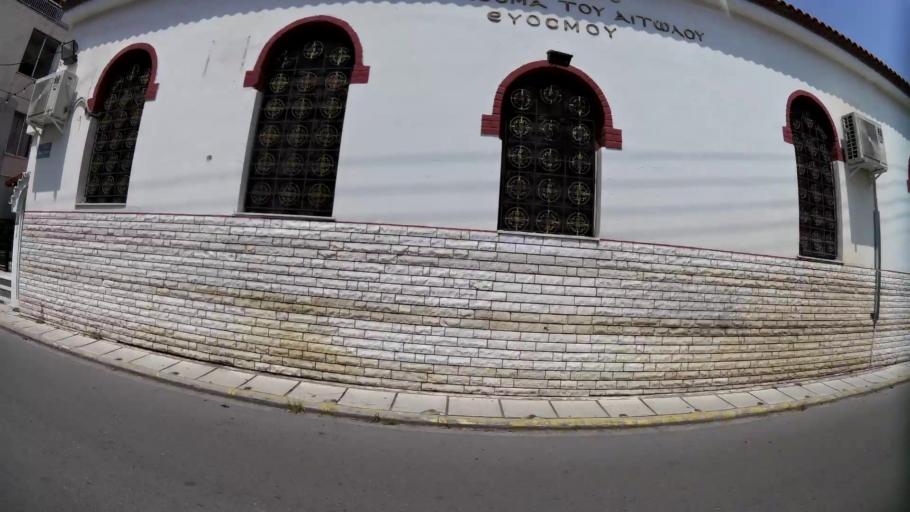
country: GR
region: Central Macedonia
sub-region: Nomos Thessalonikis
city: Evosmos
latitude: 40.6609
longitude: 22.9078
